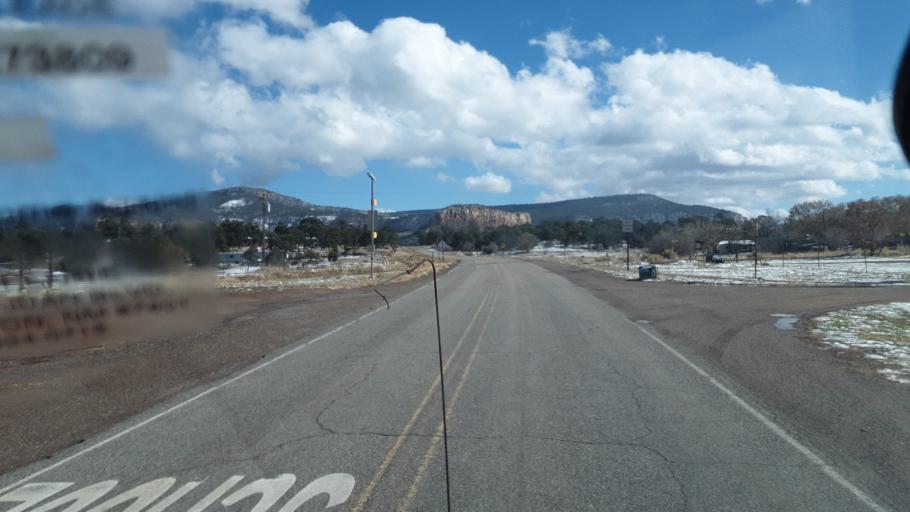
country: US
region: New Mexico
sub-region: Rio Arriba County
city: Santa Teresa
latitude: 36.2283
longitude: -106.8228
